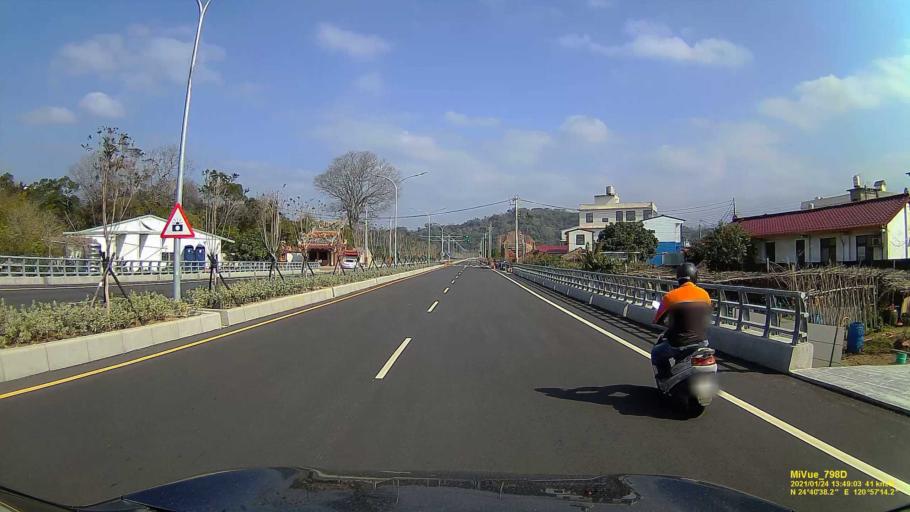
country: TW
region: Taiwan
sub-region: Hsinchu
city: Hsinchu
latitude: 24.6773
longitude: 120.9541
